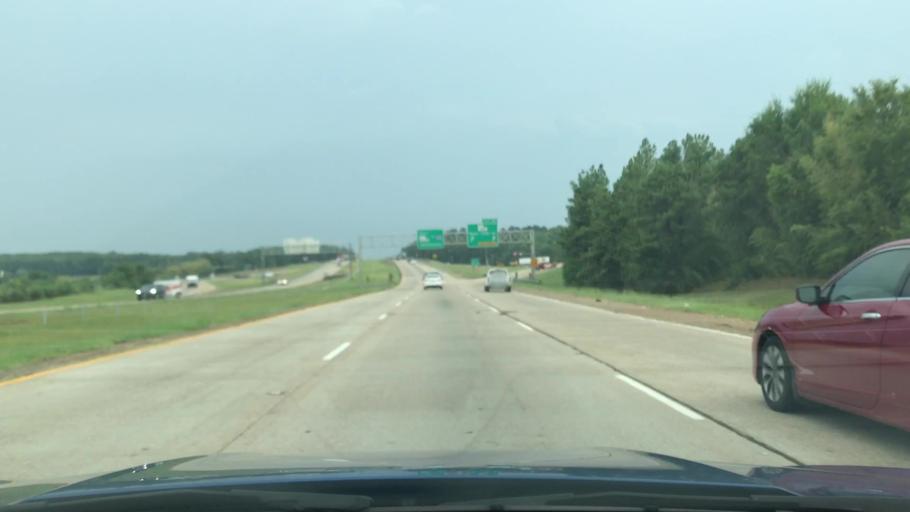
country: US
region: Louisiana
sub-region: Caddo Parish
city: Shreveport
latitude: 32.4464
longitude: -93.8429
